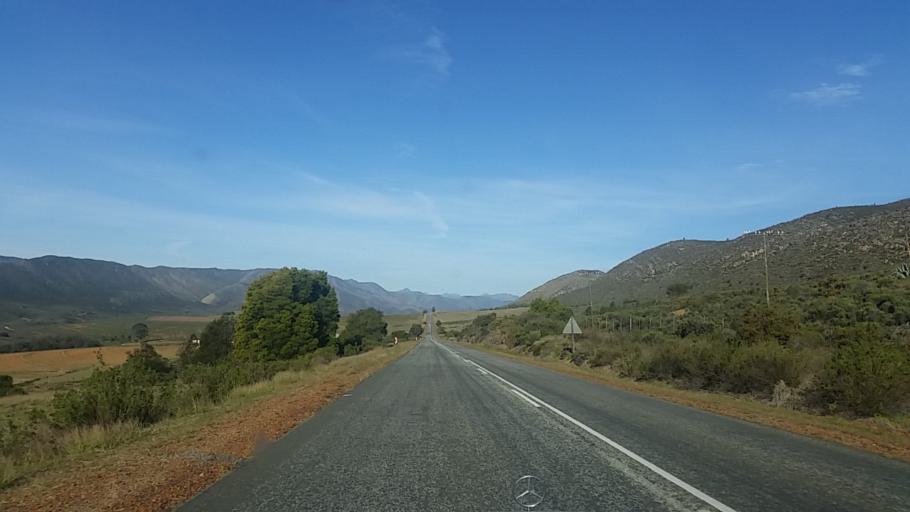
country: ZA
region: Western Cape
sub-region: Eden District Municipality
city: Knysna
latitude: -33.7728
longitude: 22.9222
